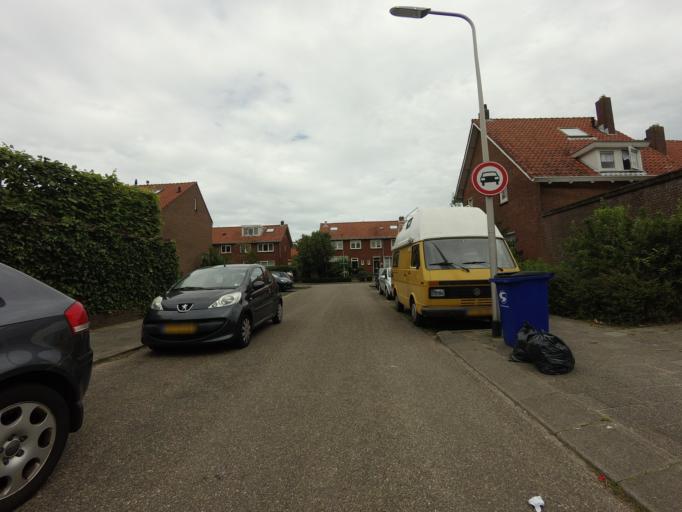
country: NL
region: North Holland
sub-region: Gemeente Uithoorn
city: Uithoorn
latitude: 52.2341
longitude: 4.8327
